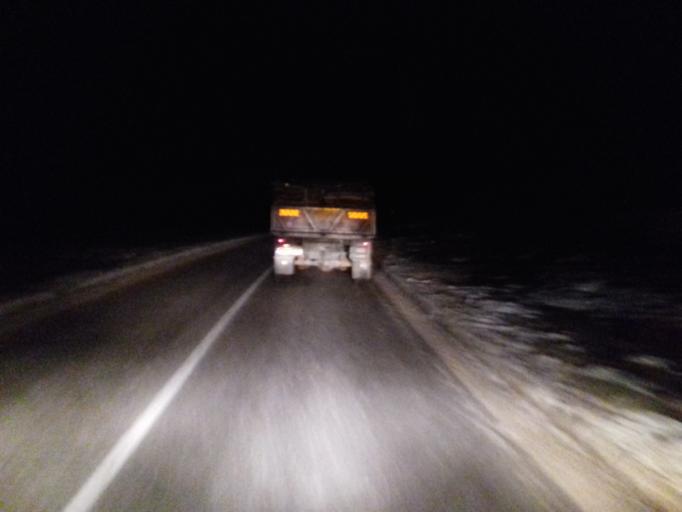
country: BA
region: Federation of Bosnia and Herzegovina
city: Gracanica
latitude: 43.7600
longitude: 18.3437
